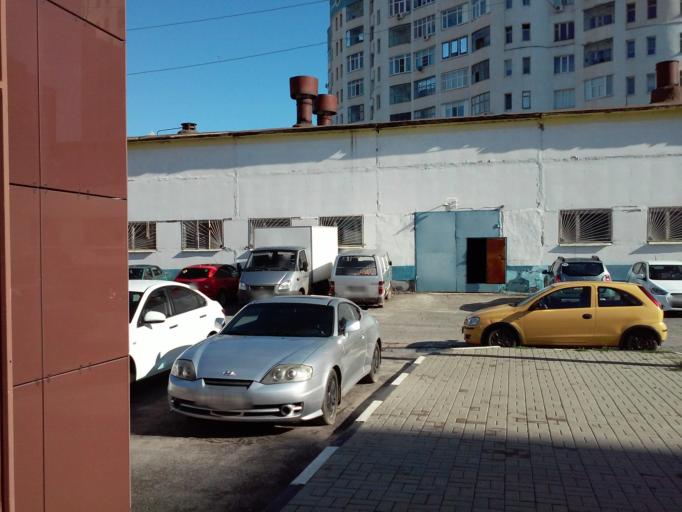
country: RU
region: Belgorod
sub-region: Belgorodskiy Rayon
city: Belgorod
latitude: 50.5567
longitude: 36.5694
